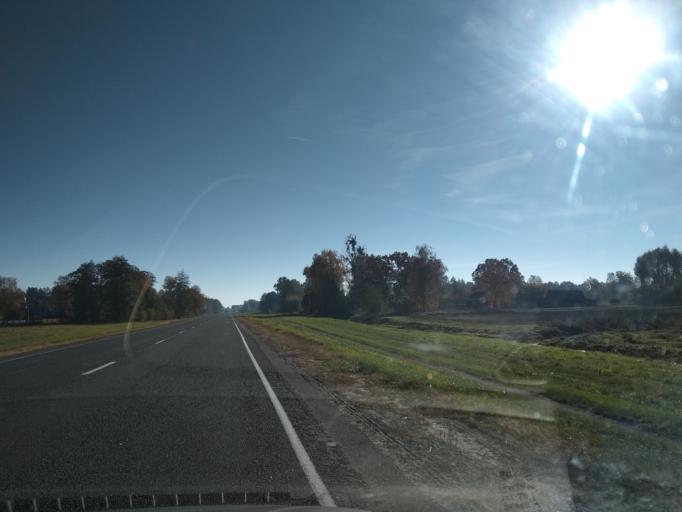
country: BY
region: Brest
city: Malaryta
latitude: 51.8319
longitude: 24.2732
